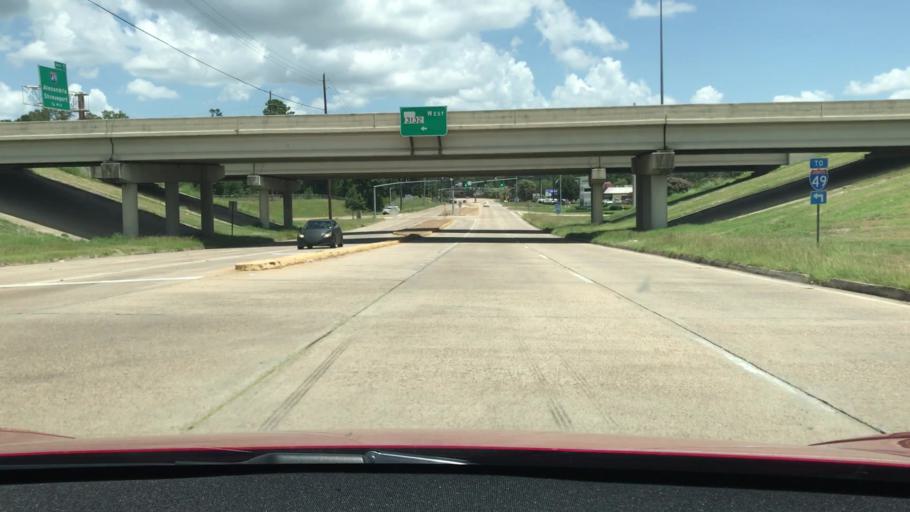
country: US
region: Louisiana
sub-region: Bossier Parish
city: Bossier City
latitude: 32.4154
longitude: -93.7375
